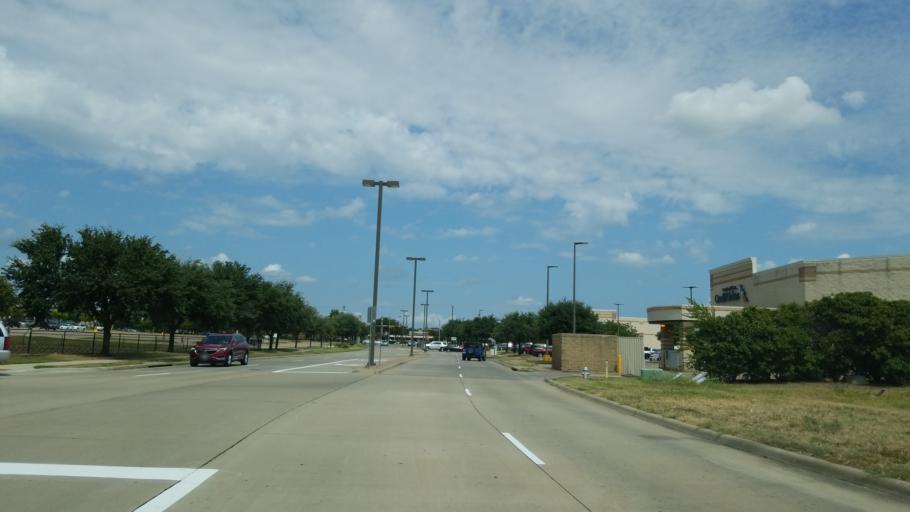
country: US
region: Texas
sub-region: Tarrant County
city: Euless
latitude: 32.8792
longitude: -97.1026
